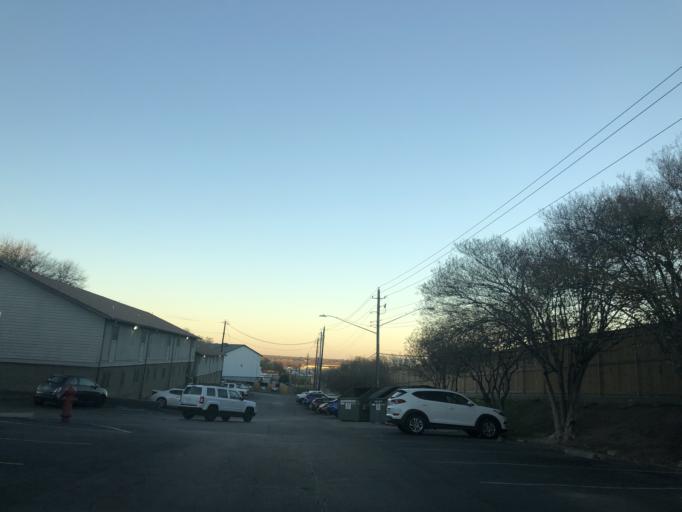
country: US
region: Texas
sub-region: Travis County
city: Austin
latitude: 30.2317
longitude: -97.7308
